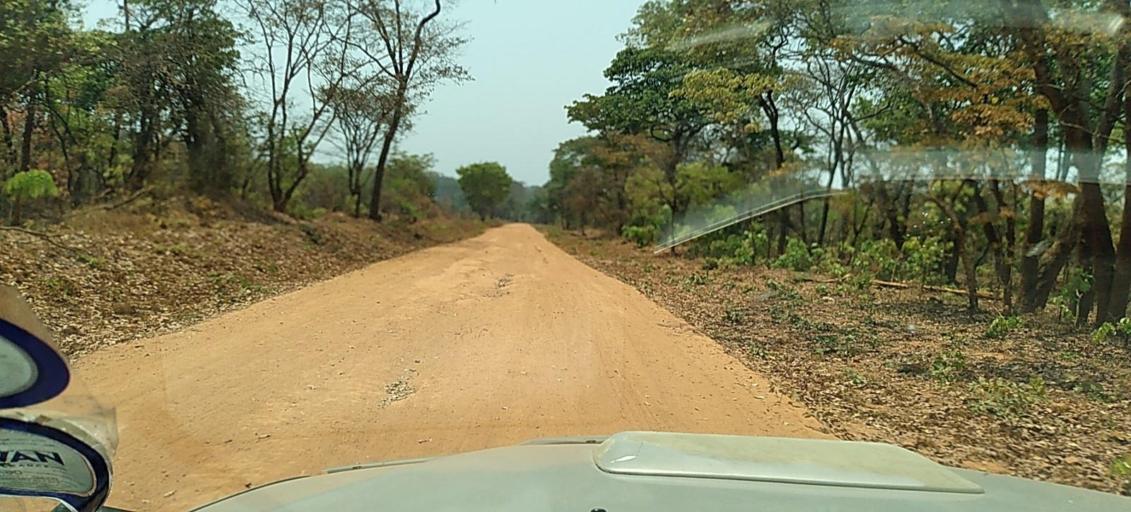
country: ZM
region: North-Western
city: Kasempa
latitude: -13.5463
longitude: 26.0374
